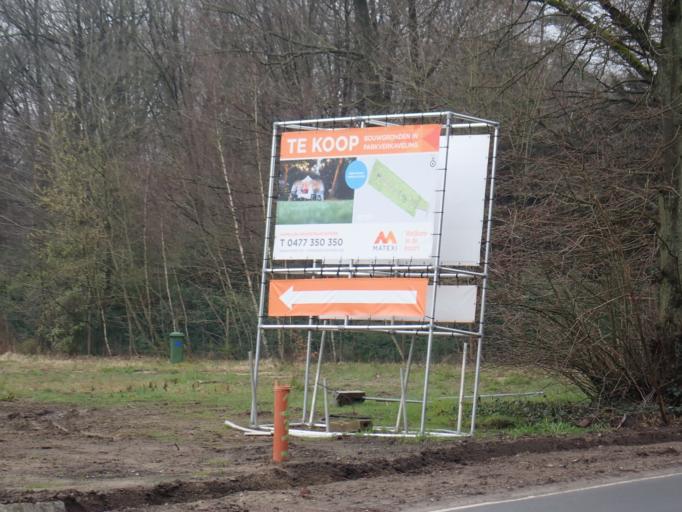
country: BE
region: Flanders
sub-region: Provincie Antwerpen
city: Kapellen
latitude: 51.3411
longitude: 4.4554
